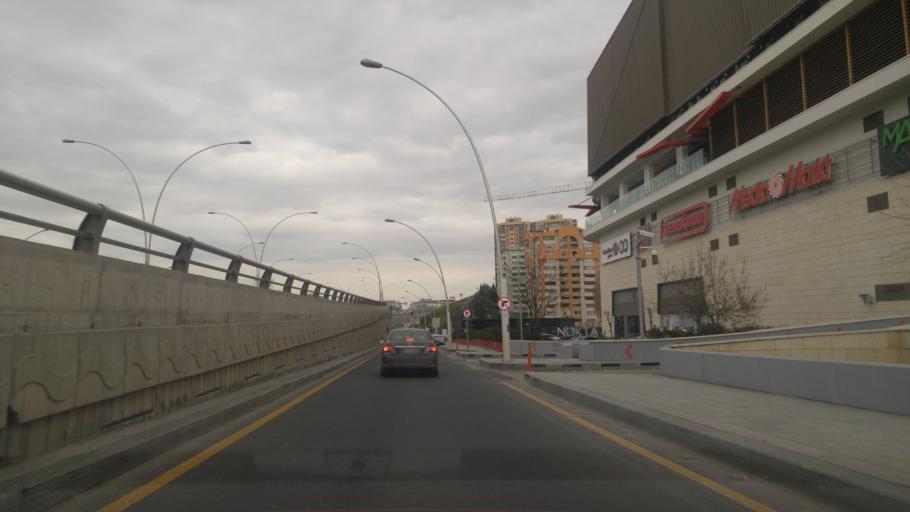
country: TR
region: Ankara
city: Etimesgut
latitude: 39.9014
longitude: 32.6903
